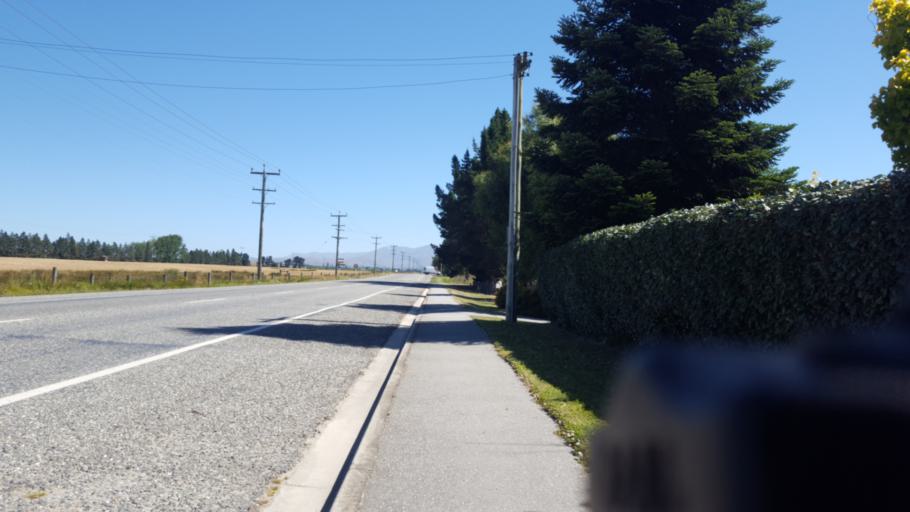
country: NZ
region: Otago
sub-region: Dunedin City
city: Dunedin
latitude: -45.1245
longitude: 170.0954
